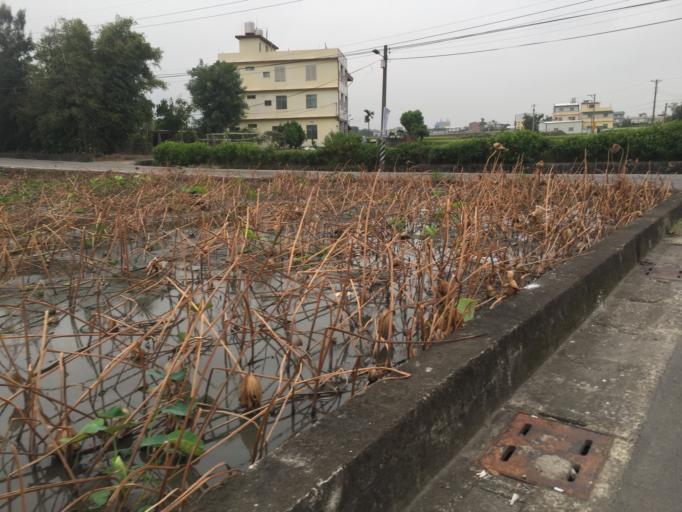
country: TW
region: Taiwan
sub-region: Miaoli
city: Miaoli
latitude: 24.5854
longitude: 120.8314
